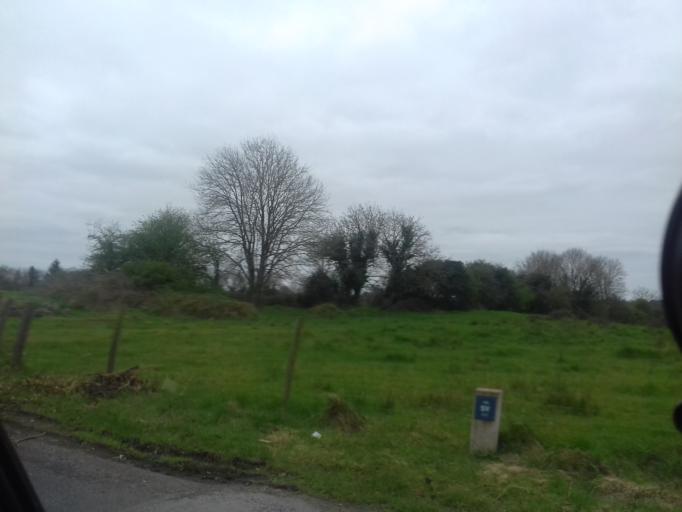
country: IE
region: Leinster
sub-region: An Iarmhi
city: An Muileann gCearr
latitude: 53.5240
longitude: -7.3143
